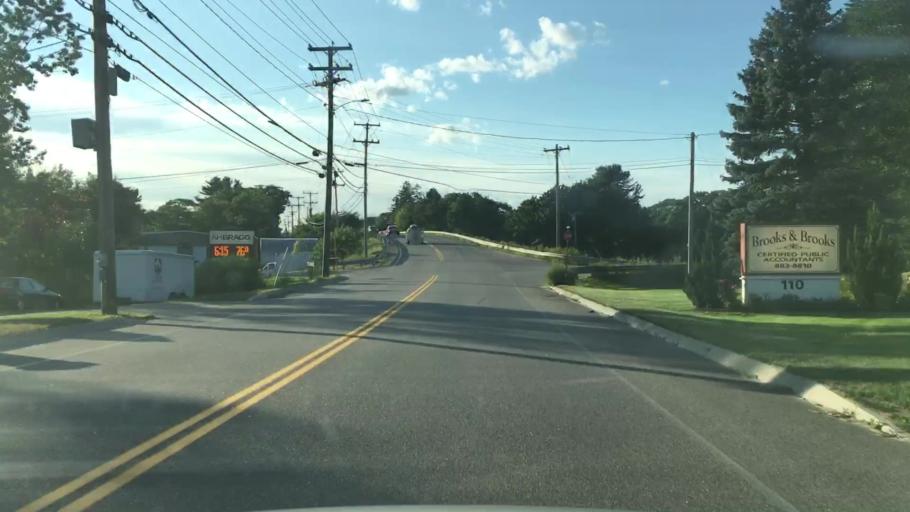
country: US
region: Maine
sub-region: Cumberland County
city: Scarborough
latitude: 43.6016
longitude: -70.3001
